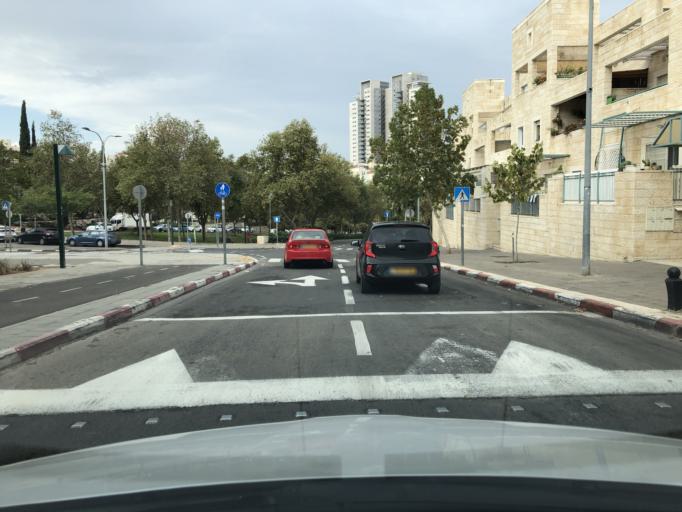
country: IL
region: Central District
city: Modiin
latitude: 31.9141
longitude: 35.0062
